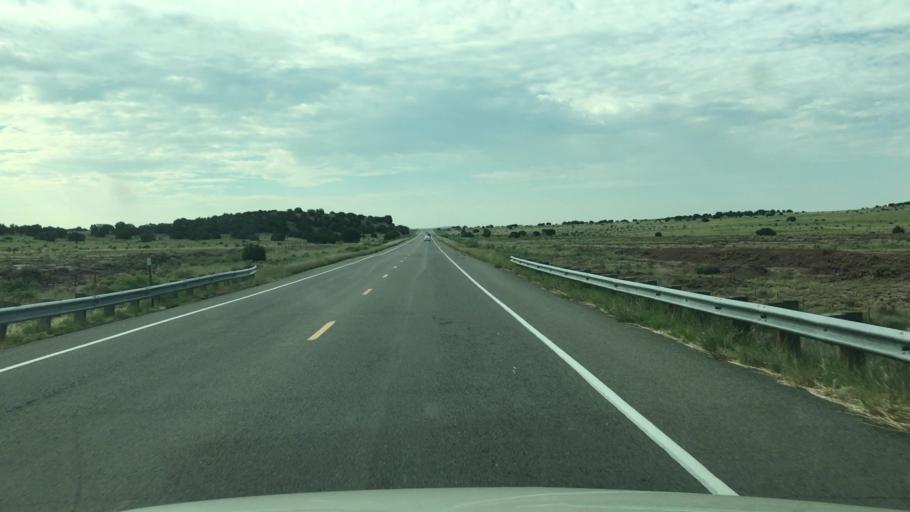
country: US
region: New Mexico
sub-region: Santa Fe County
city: Eldorado at Santa Fe
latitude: 35.4368
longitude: -105.8827
